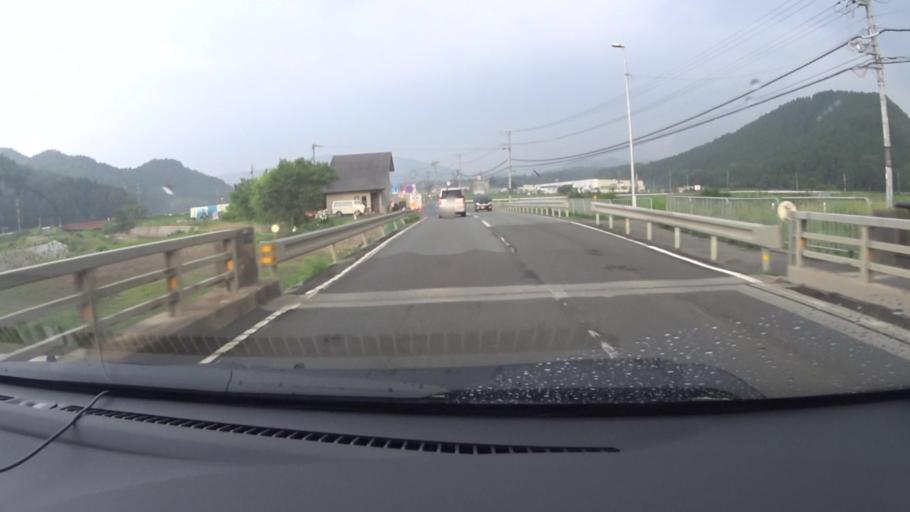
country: JP
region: Kyoto
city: Ayabe
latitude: 35.1851
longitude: 135.4179
